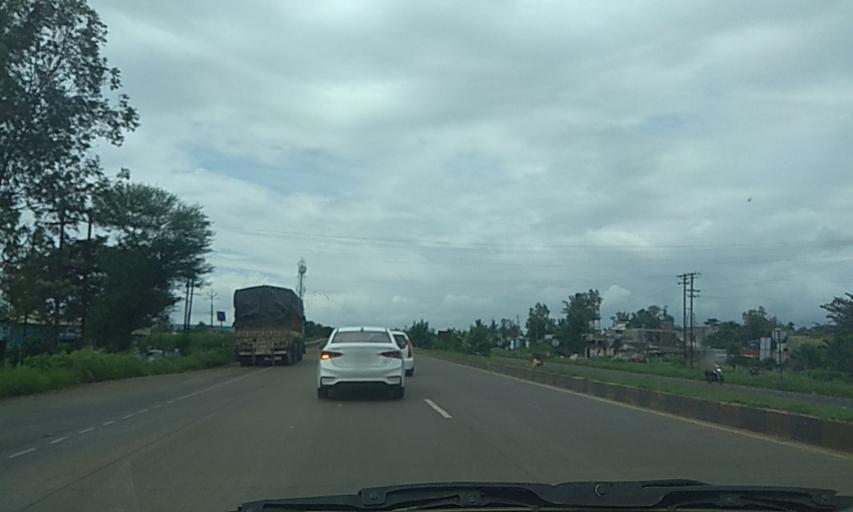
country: IN
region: Maharashtra
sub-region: Kolhapur
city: Kagal
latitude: 16.5668
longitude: 74.3156
